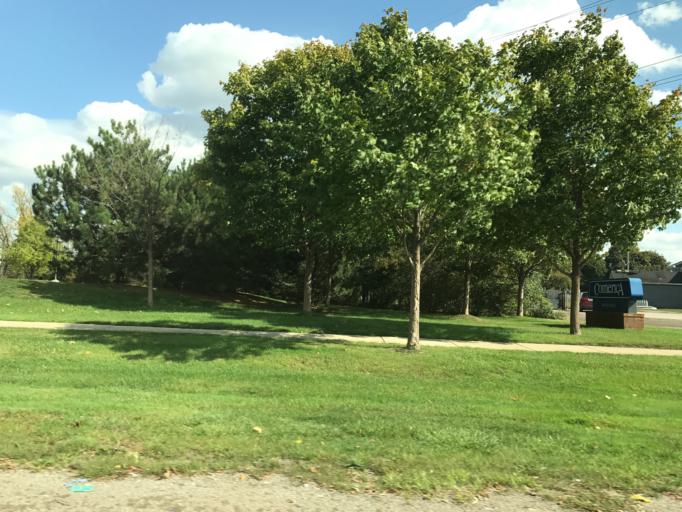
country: US
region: Michigan
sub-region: Oakland County
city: South Lyon
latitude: 42.5119
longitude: -83.6157
